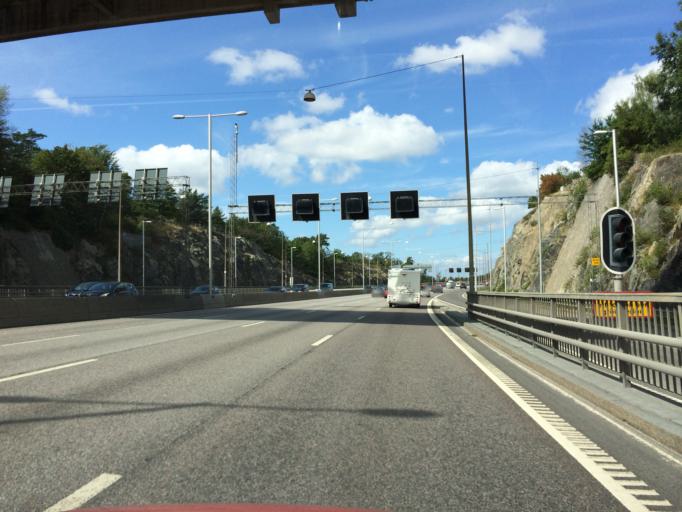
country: SE
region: Stockholm
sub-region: Stockholms Kommun
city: Arsta
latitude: 59.3075
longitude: 18.0110
